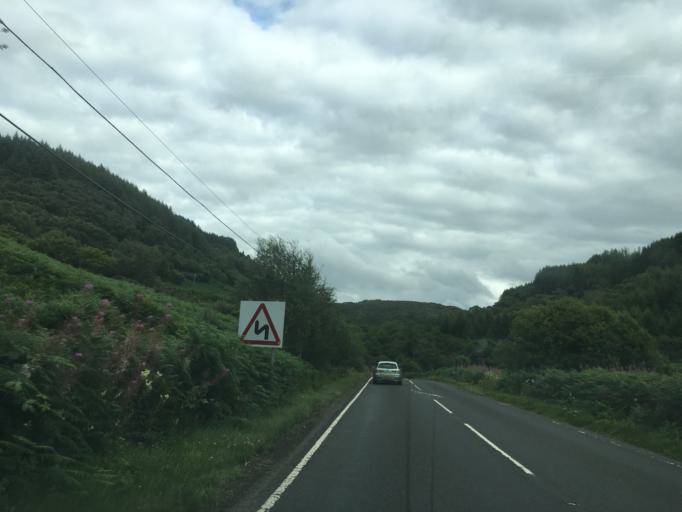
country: GB
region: Scotland
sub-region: Argyll and Bute
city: Oban
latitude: 56.3182
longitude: -5.4899
